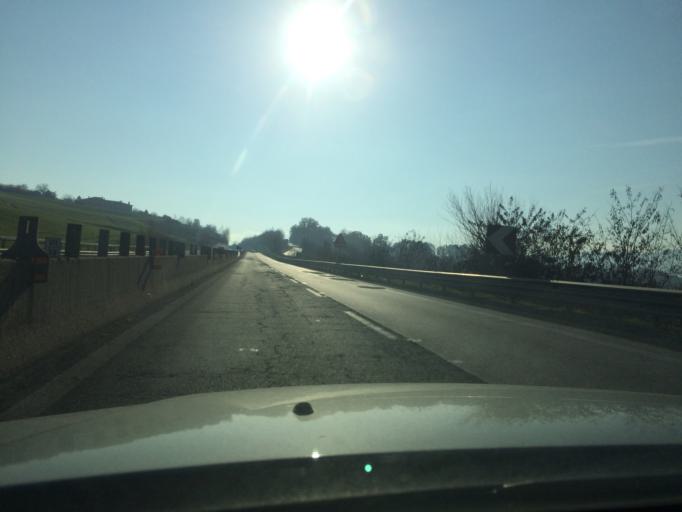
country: IT
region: Umbria
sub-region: Provincia di Perugia
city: Ponterio-Pian di Porto
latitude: 42.8307
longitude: 12.4002
